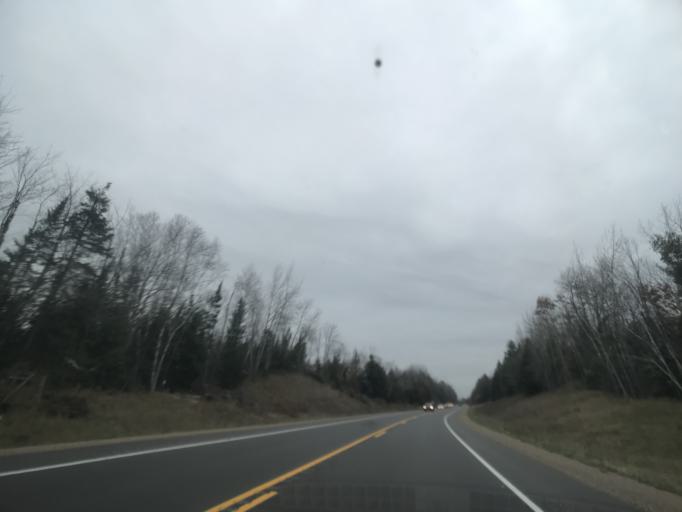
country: US
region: Wisconsin
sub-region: Menominee County
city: Legend Lake
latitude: 45.2642
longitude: -88.5128
